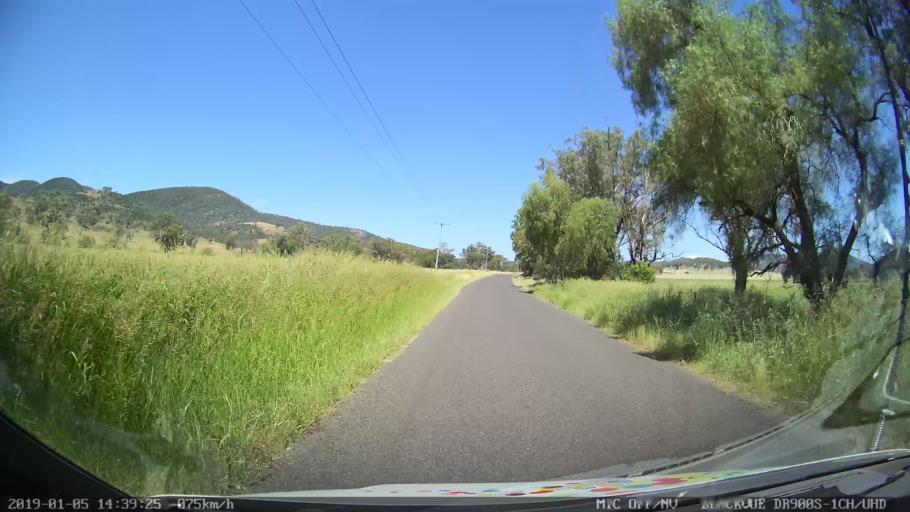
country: AU
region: New South Wales
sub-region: Tamworth Municipality
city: Phillip
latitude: -31.2544
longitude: 150.7000
